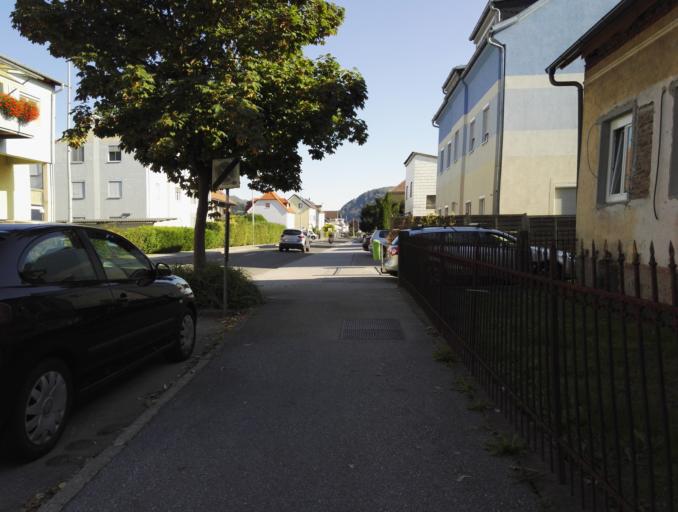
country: AT
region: Styria
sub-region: Politischer Bezirk Graz-Umgebung
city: Gratkorn
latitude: 47.1315
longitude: 15.3404
